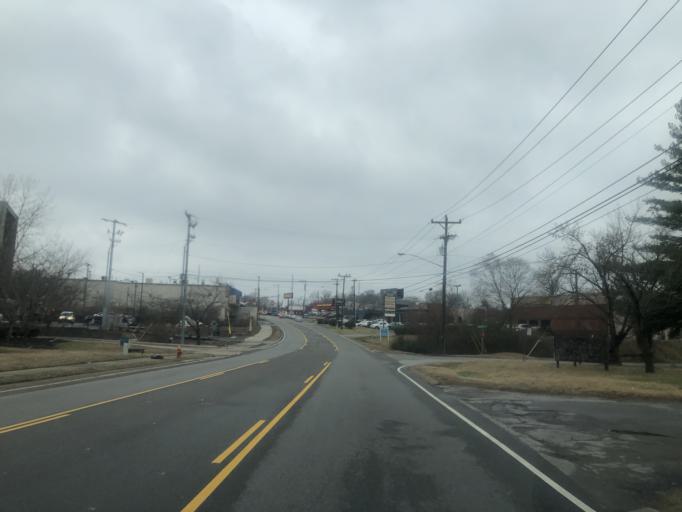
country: US
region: Tennessee
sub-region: Davidson County
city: Lakewood
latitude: 36.1478
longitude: -86.6635
